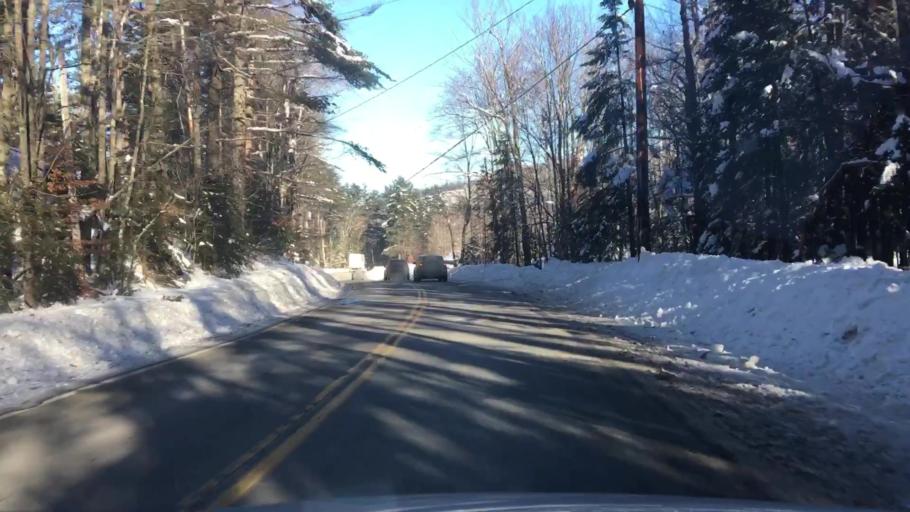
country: US
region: Maine
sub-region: Oxford County
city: West Paris
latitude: 44.4010
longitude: -70.6340
